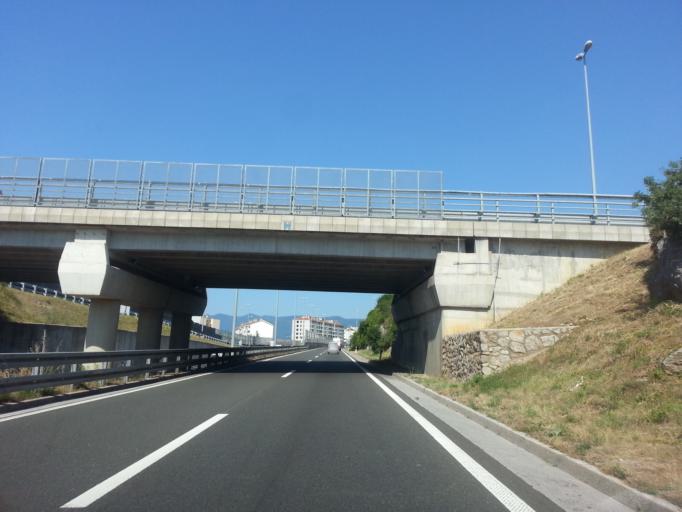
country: HR
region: Primorsko-Goranska
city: Rijeka
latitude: 45.3435
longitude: 14.4047
